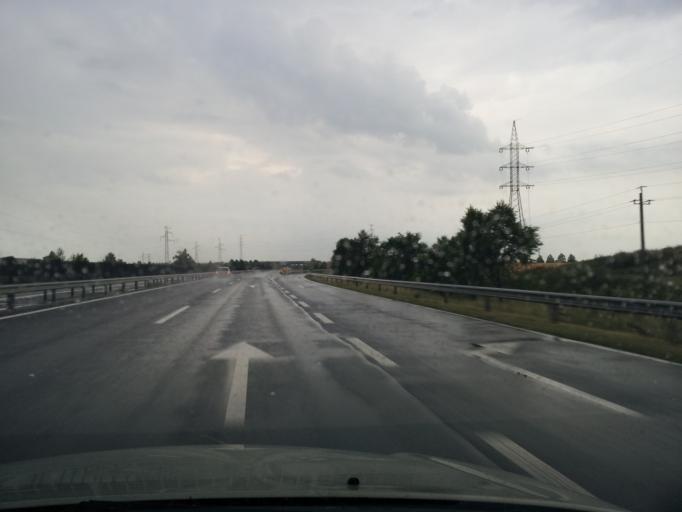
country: HU
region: Borsod-Abauj-Zemplen
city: Onod
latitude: 47.9846
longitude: 20.8970
